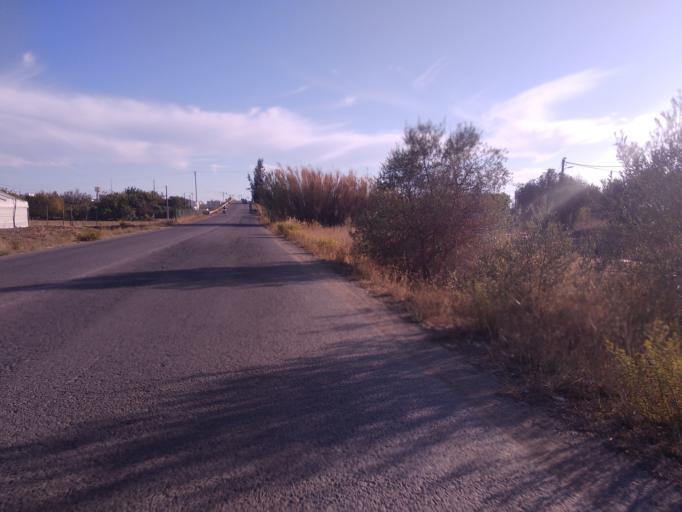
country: PT
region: Faro
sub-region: Faro
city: Faro
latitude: 37.0443
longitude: -7.9380
